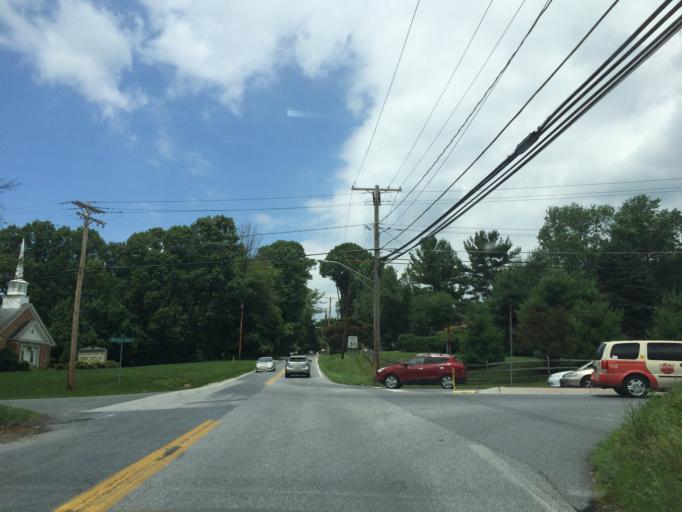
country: US
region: Maryland
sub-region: Baltimore County
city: Randallstown
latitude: 39.3547
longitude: -76.7954
